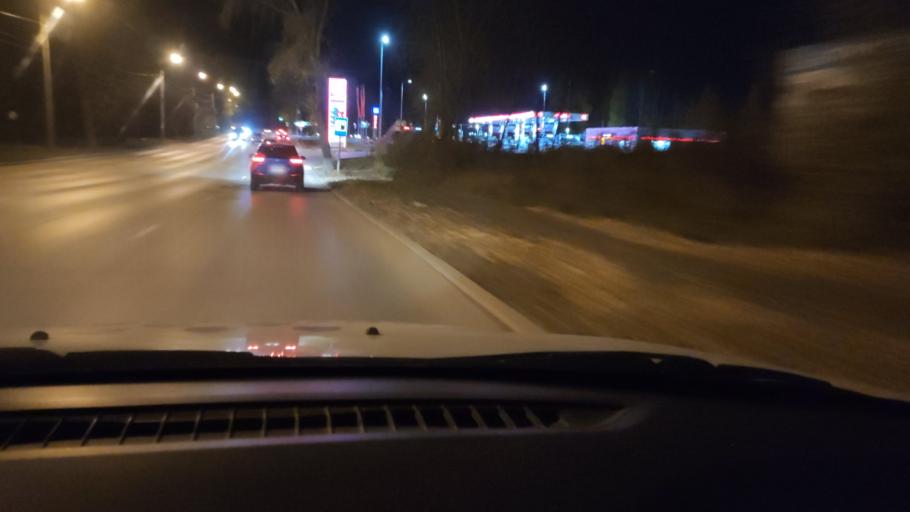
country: RU
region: Perm
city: Froly
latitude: 57.9559
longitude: 56.2420
